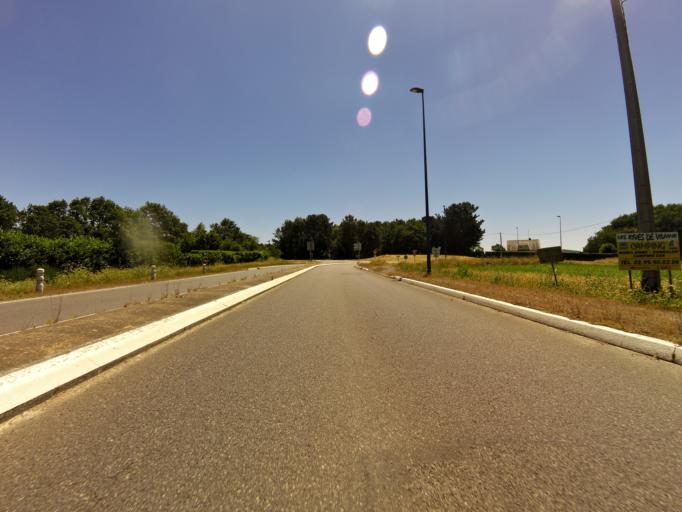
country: FR
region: Brittany
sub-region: Departement du Morbihan
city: Ferel
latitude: 47.4840
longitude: -2.3860
